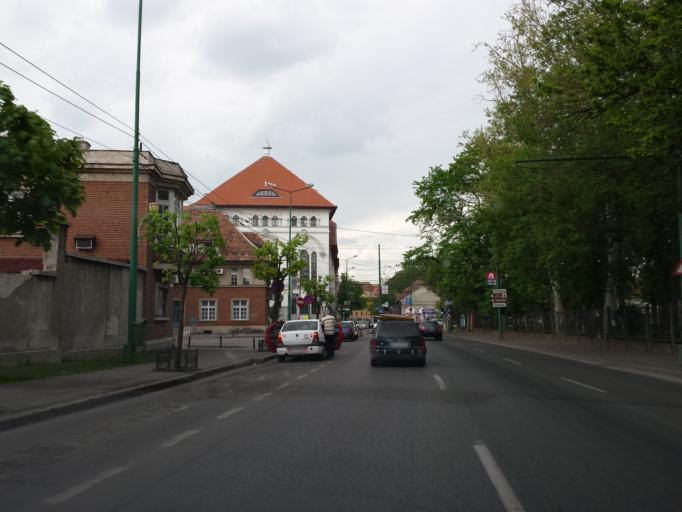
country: RO
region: Timis
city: Timisoara
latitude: 45.7501
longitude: 21.2265
